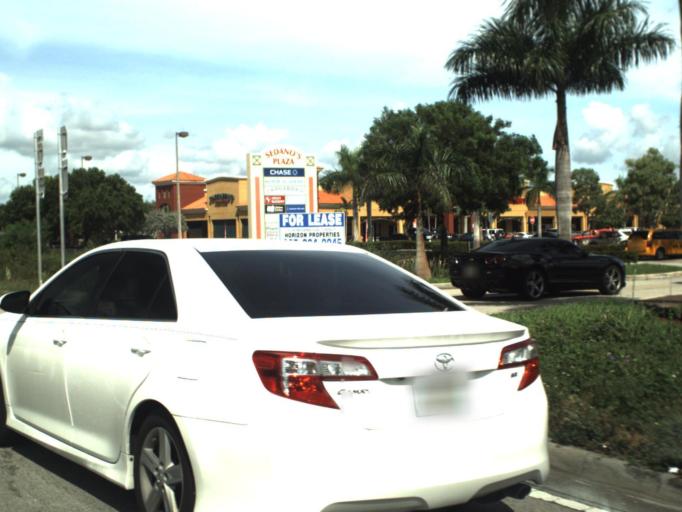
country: US
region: Florida
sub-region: Miami-Dade County
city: Palm Springs North
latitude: 25.9424
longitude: -80.3434
